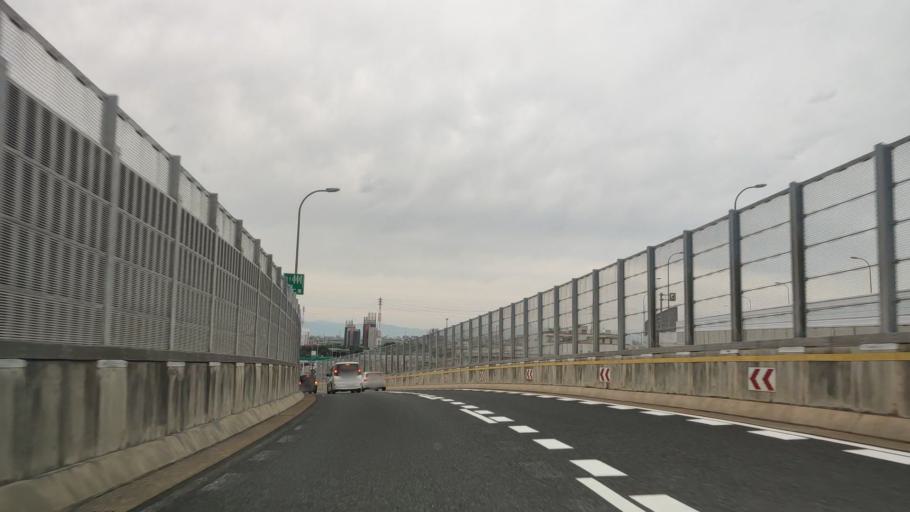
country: JP
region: Aichi
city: Iwakura
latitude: 35.2700
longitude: 136.8322
